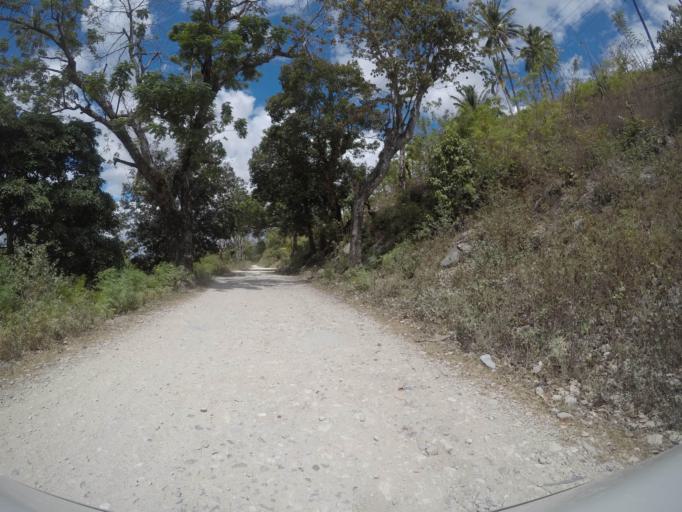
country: TL
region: Baucau
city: Baucau
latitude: -8.5271
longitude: 126.6945
